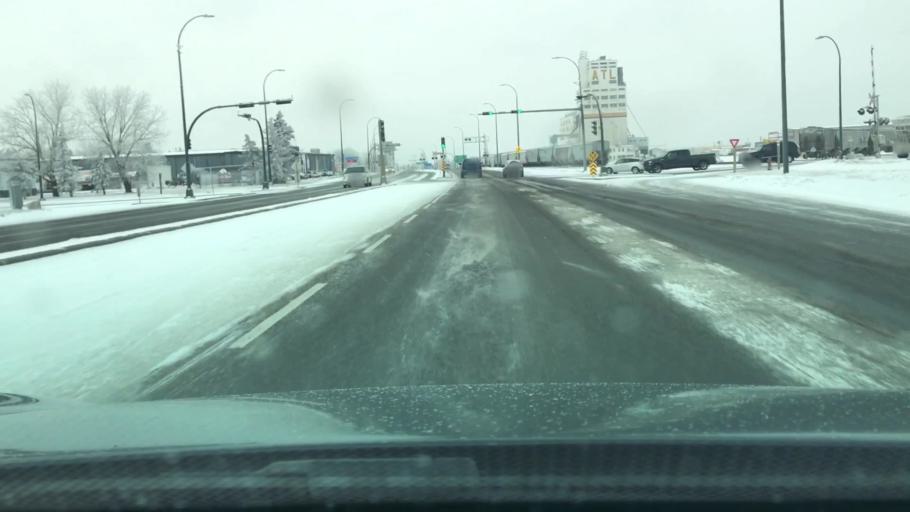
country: CA
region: Alberta
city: Lethbridge
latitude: 49.6983
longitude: -112.7955
